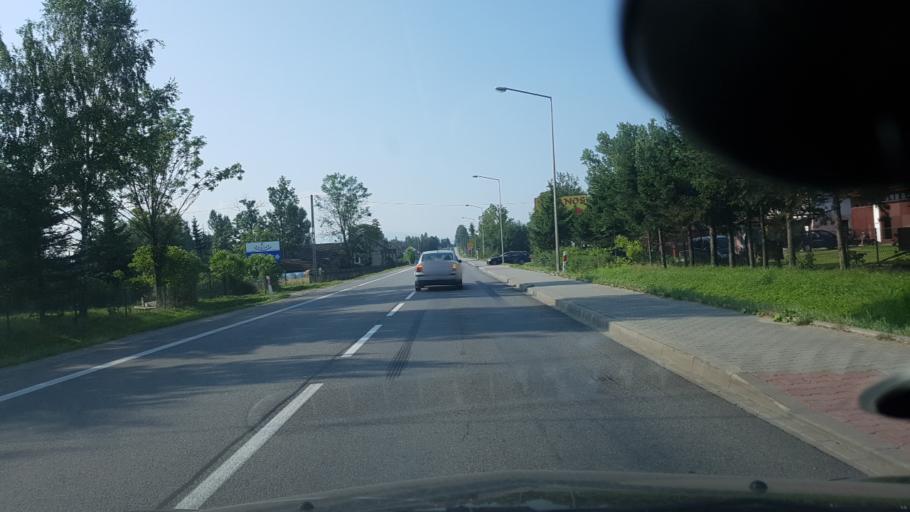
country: PL
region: Lesser Poland Voivodeship
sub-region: Powiat nowotarski
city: Jablonka
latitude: 49.4655
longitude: 19.6915
